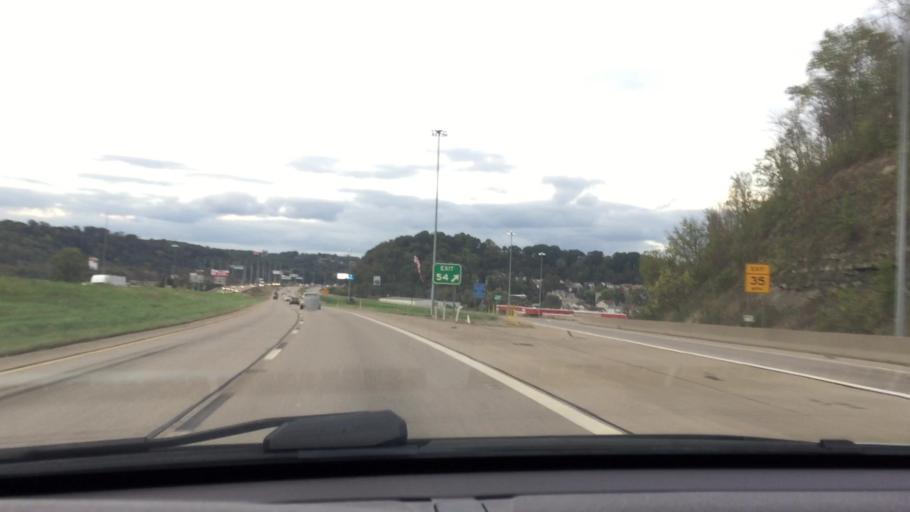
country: US
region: Pennsylvania
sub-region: Allegheny County
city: Bridgeville
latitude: 40.3515
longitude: -80.1172
